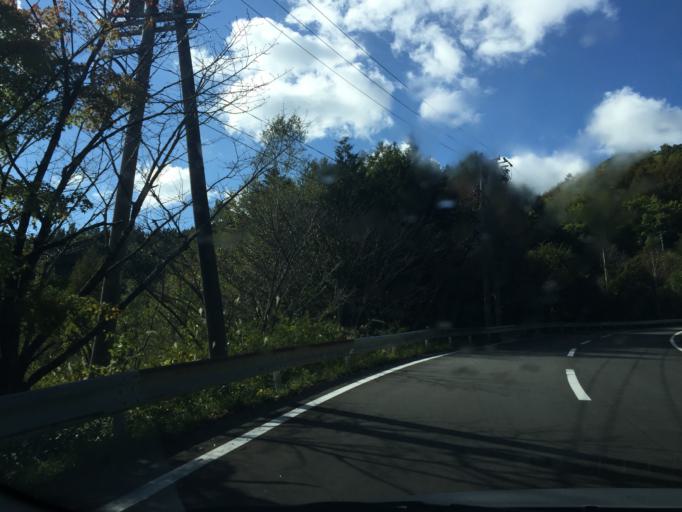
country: JP
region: Gifu
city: Nakatsugawa
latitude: 35.2984
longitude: 137.6768
